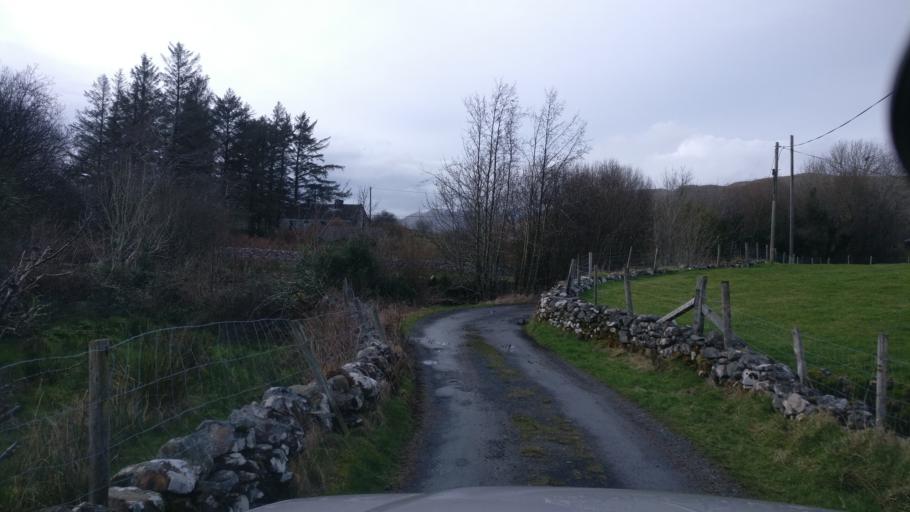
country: IE
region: Connaught
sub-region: County Galway
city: Oughterard
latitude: 53.5552
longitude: -9.4415
